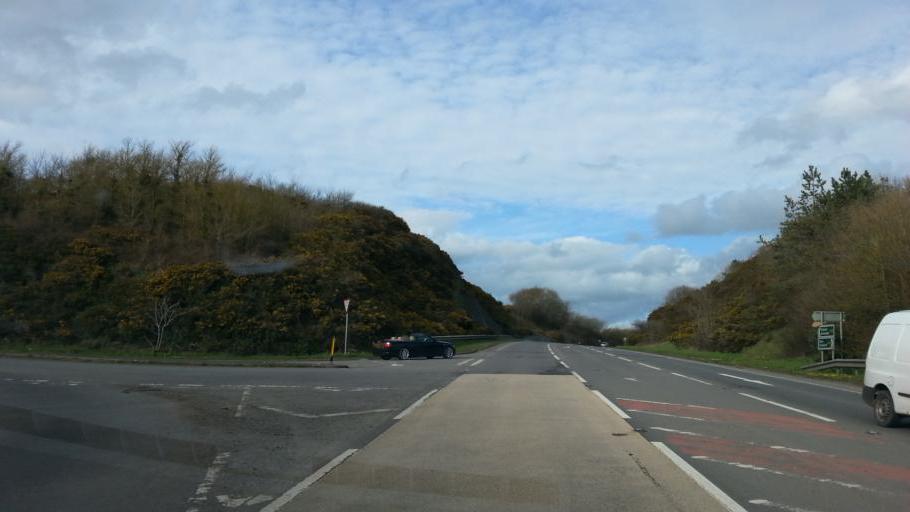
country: GB
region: England
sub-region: Devon
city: Northam
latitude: 51.0259
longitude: -4.2310
